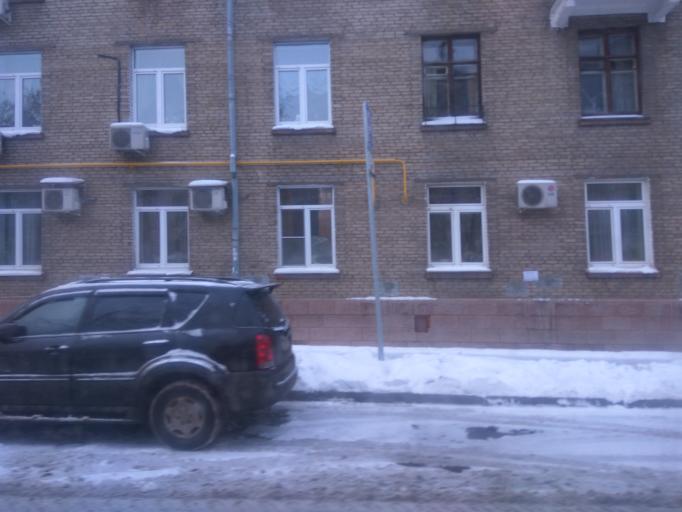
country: RU
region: Moscow
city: Ostankinskiy
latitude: 55.8178
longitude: 37.5921
